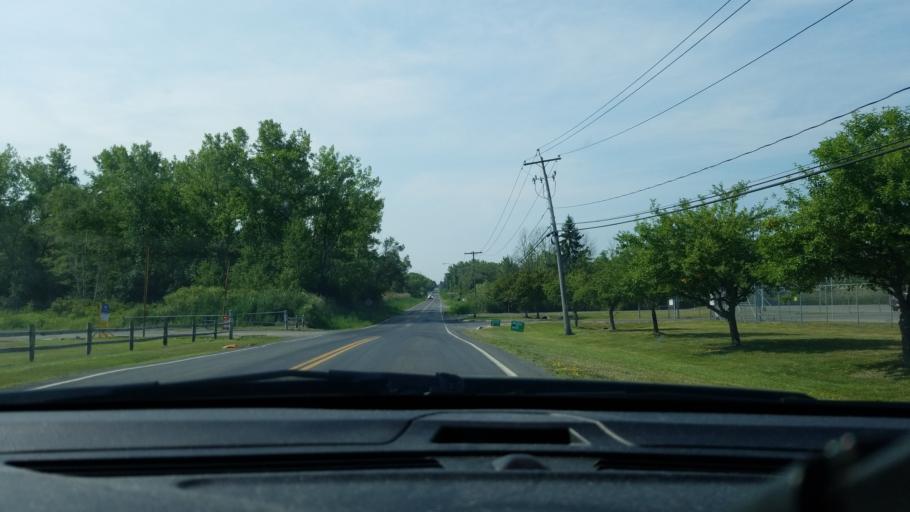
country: US
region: New York
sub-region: Onondaga County
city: East Syracuse
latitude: 43.1203
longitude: -76.0738
